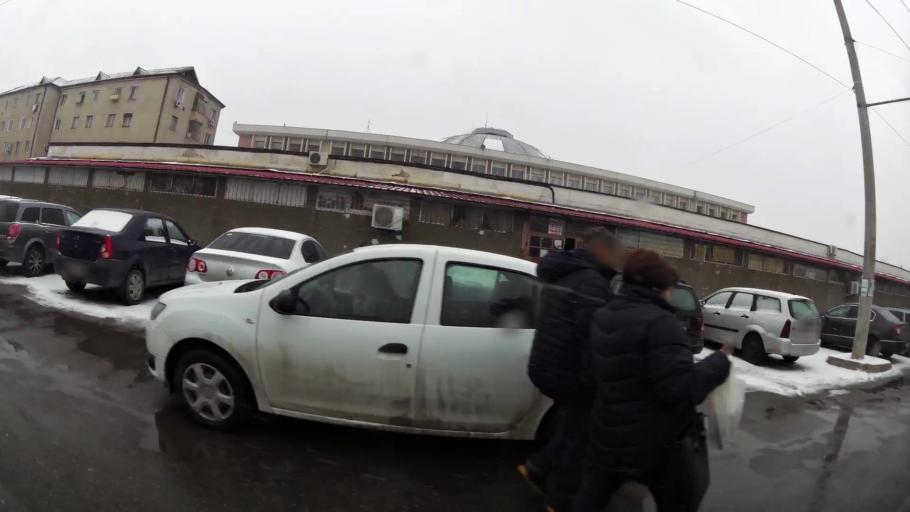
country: RO
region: Dambovita
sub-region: Municipiul Targoviste
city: Targoviste
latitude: 44.9185
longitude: 25.4504
